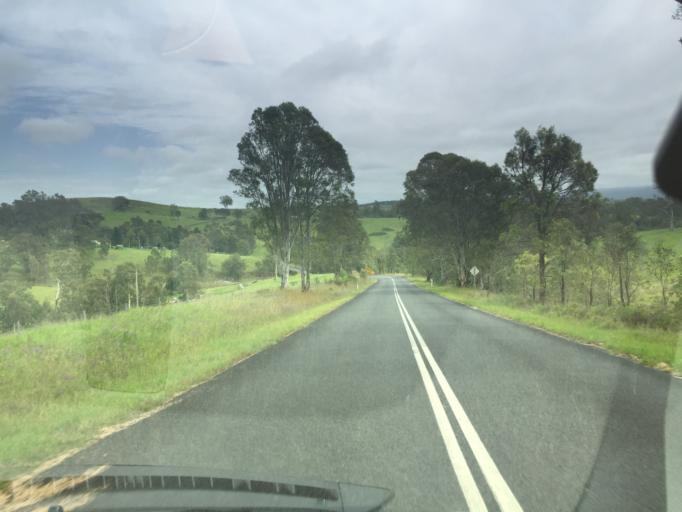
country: AU
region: New South Wales
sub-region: Bega Valley
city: Bega
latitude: -36.7150
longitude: 149.5982
